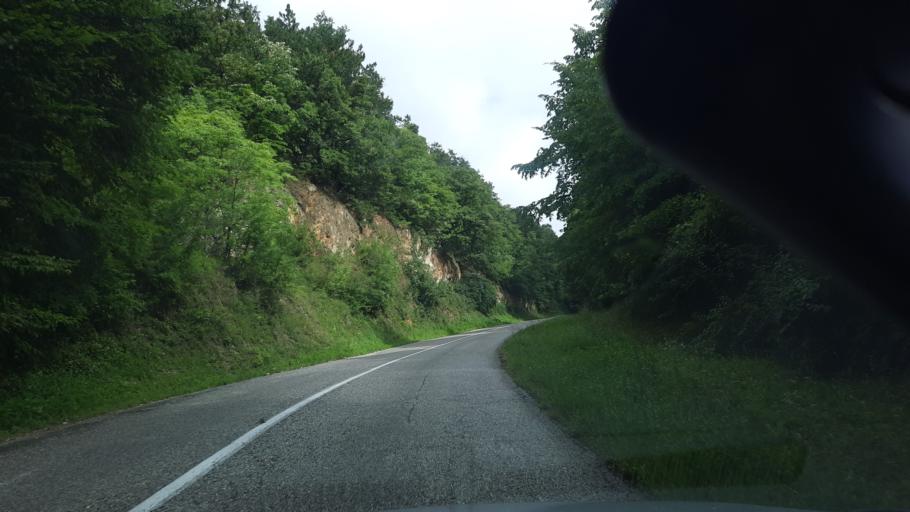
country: RS
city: Glozan
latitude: 45.1391
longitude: 19.5795
